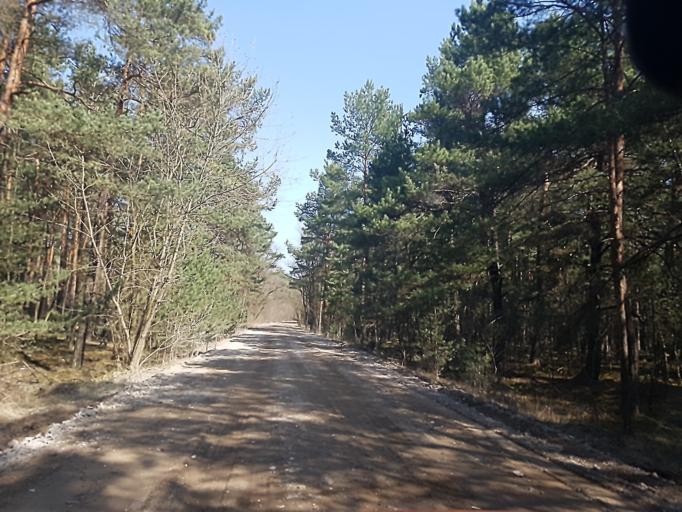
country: DE
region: Brandenburg
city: Tschernitz
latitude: 51.6663
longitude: 14.5664
